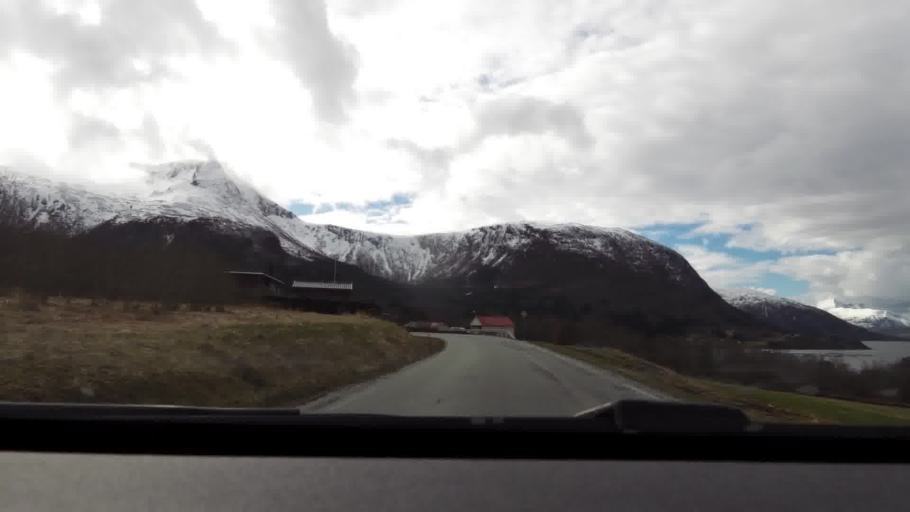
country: NO
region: More og Romsdal
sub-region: Gjemnes
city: Batnfjordsora
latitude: 62.9363
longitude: 7.6027
